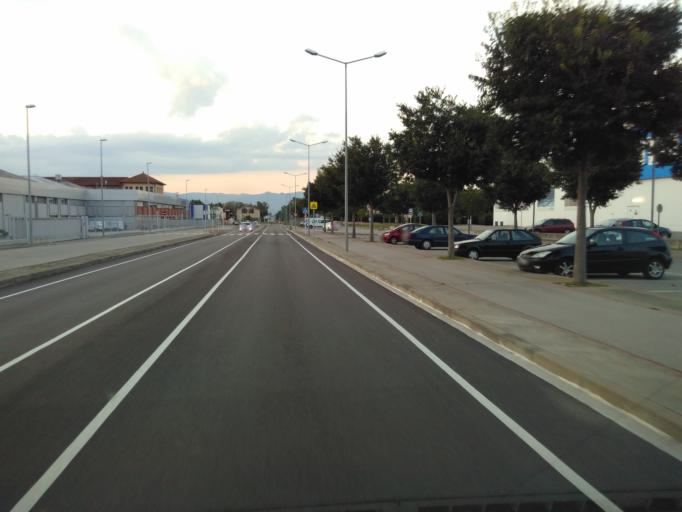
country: ES
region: Catalonia
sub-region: Provincia de Barcelona
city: Vic
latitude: 41.9446
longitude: 2.2581
